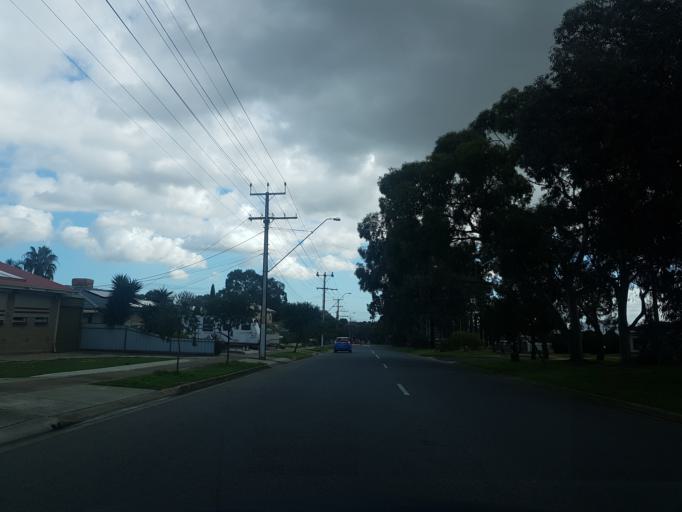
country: AU
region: South Australia
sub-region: Salisbury
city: Ingle Farm
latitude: -34.8184
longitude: 138.6468
